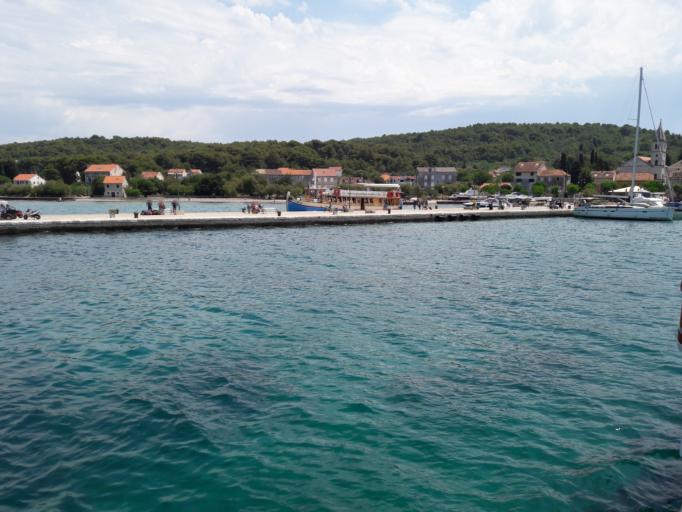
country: HR
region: Sibensko-Kniniska
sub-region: Grad Sibenik
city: Sibenik
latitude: 43.6992
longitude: 15.8328
